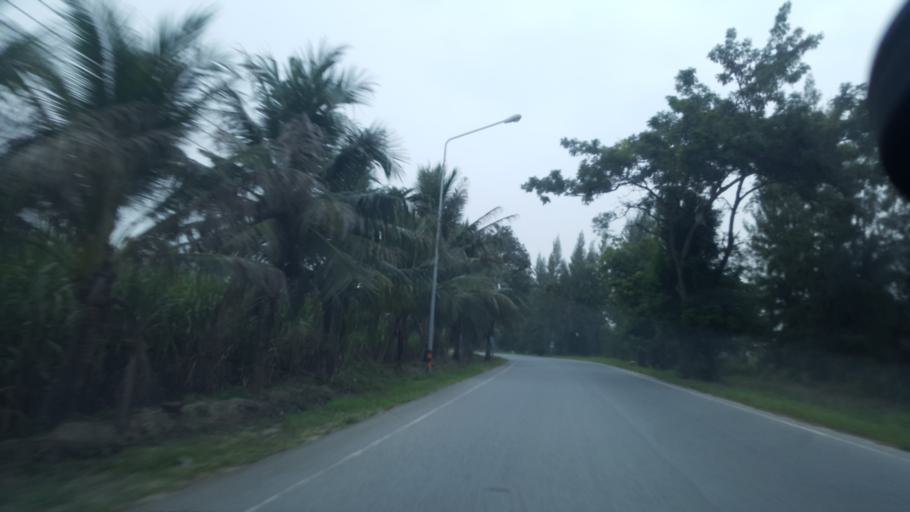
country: TH
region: Chon Buri
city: Si Racha
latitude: 13.2362
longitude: 101.0163
